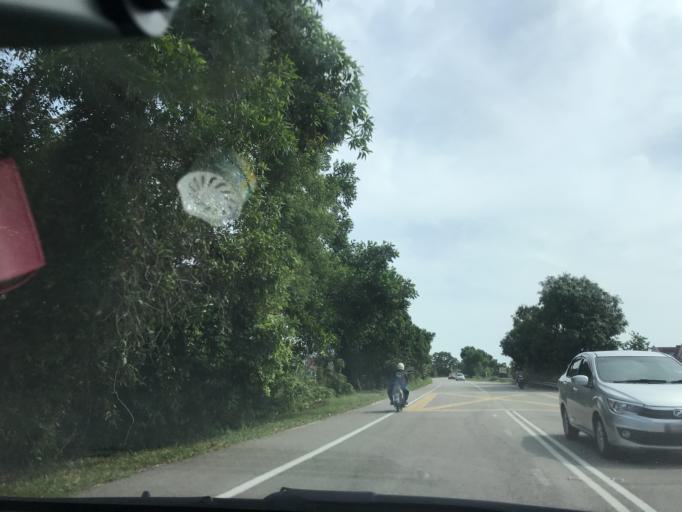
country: MY
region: Kelantan
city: Tumpat
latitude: 6.1970
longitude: 102.1554
